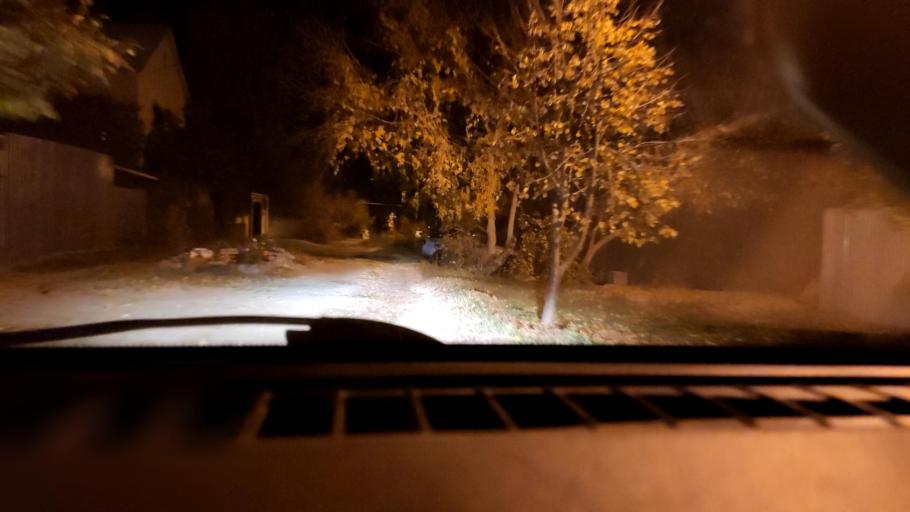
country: RU
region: Samara
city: Samara
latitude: 53.2259
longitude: 50.1551
